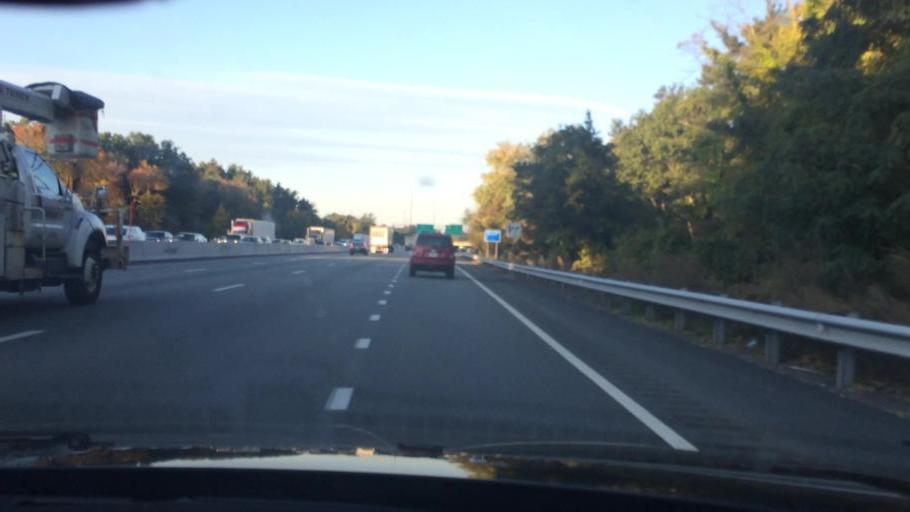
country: US
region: Massachusetts
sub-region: Middlesex County
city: Lowell
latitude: 42.6105
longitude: -71.3103
